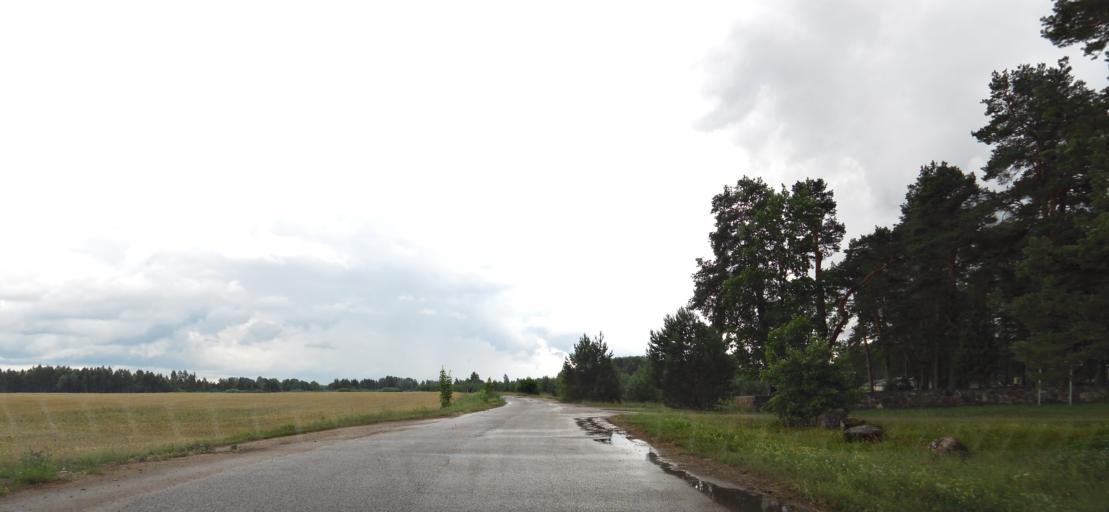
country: LT
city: Vabalninkas
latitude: 55.8866
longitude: 24.7695
